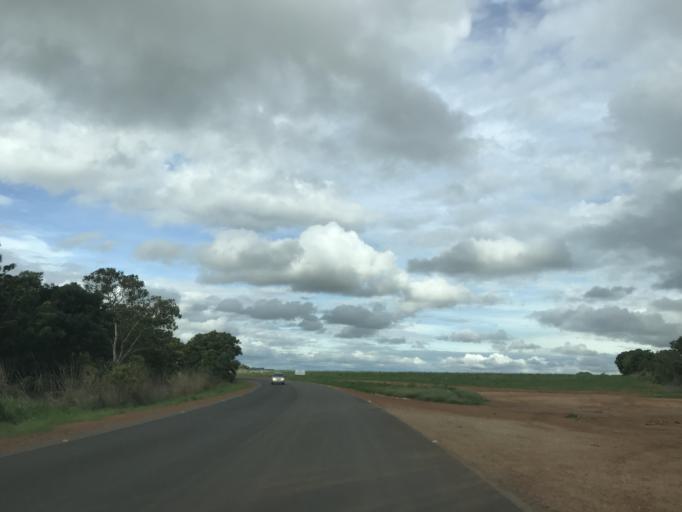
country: BR
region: Goias
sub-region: Vianopolis
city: Vianopolis
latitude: -16.9677
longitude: -48.6019
